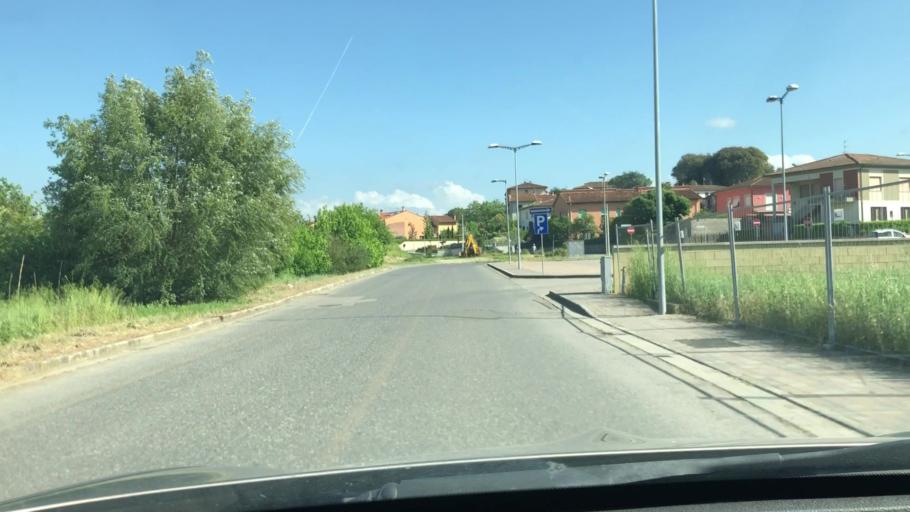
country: IT
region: Tuscany
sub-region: Province of Pisa
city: Capannoli
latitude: 43.5889
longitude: 10.6754
